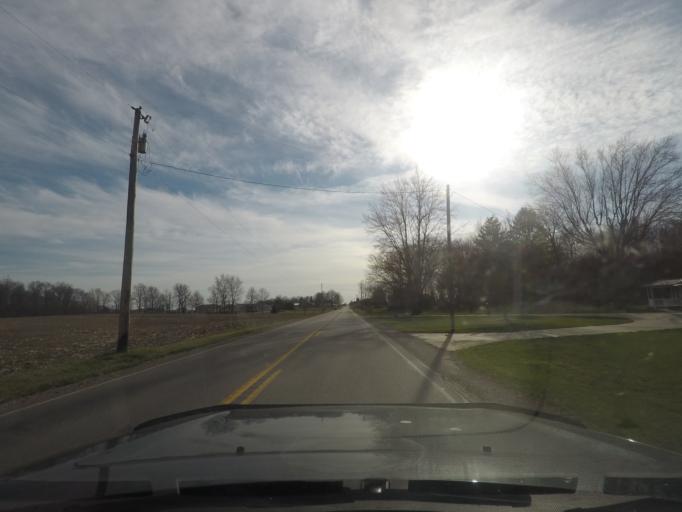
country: US
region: Indiana
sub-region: Elkhart County
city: Wakarusa
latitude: 41.5299
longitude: -85.9522
